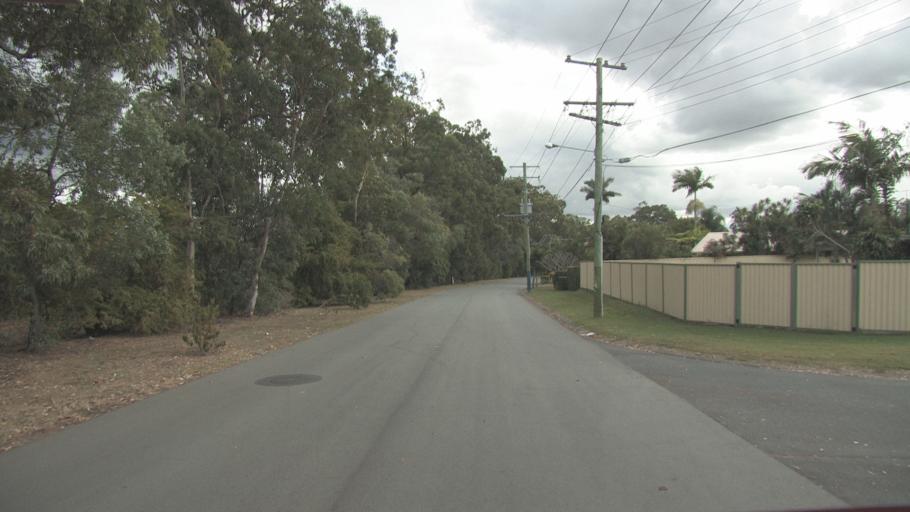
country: AU
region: Queensland
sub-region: Logan
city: Park Ridge South
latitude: -27.6655
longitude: 153.0199
